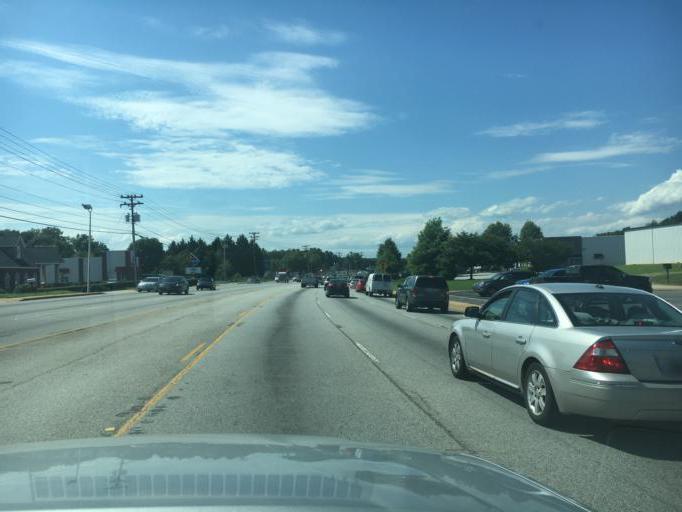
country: US
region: South Carolina
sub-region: Greenville County
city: Welcome
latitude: 34.8120
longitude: -82.4395
